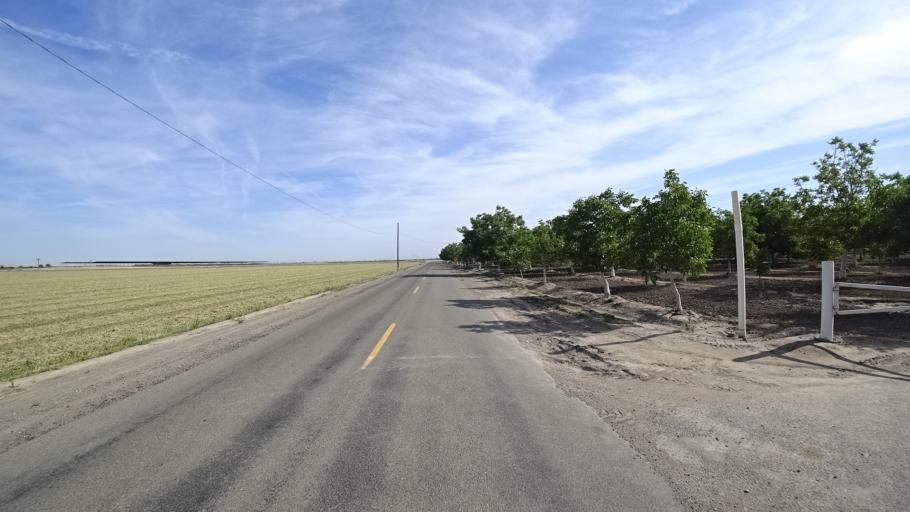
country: US
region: California
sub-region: Tulare County
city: Goshen
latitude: 36.3455
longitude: -119.4930
